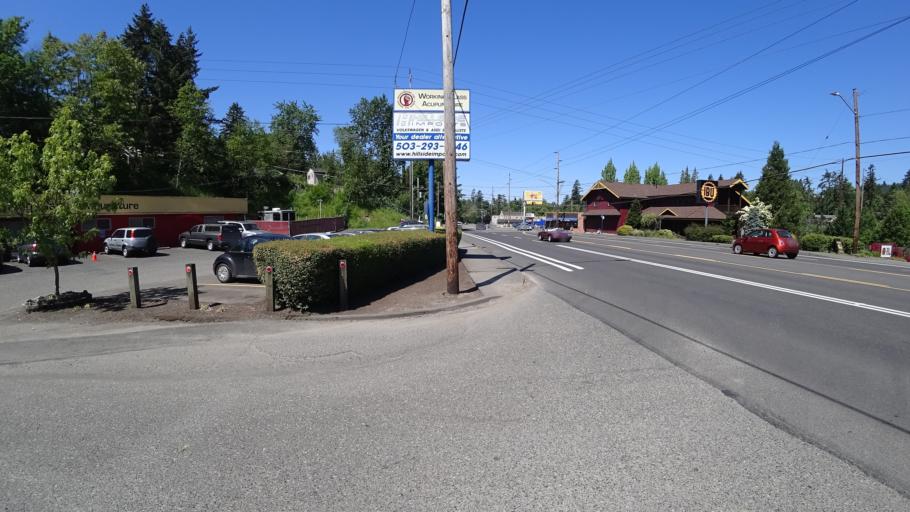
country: US
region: Oregon
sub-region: Washington County
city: Raleigh Hills
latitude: 45.4856
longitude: -122.7224
